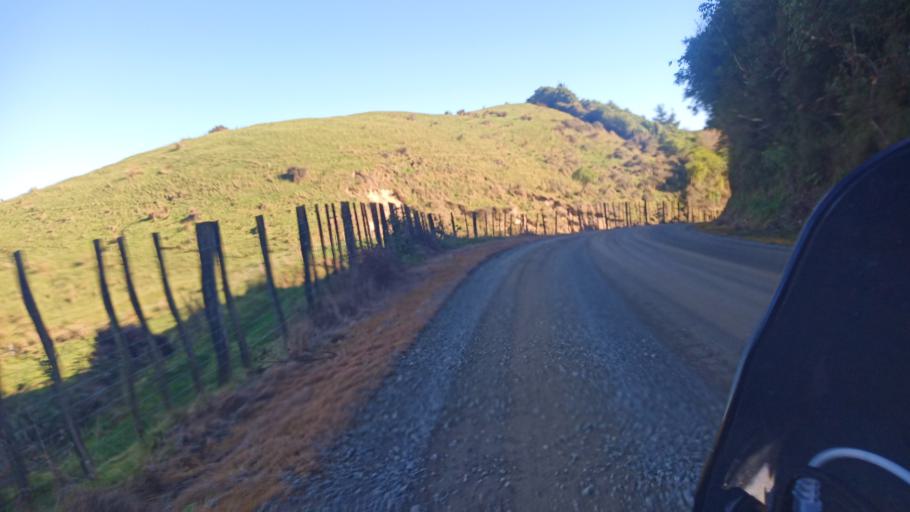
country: NZ
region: Hawke's Bay
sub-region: Wairoa District
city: Wairoa
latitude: -38.7952
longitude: 177.2837
